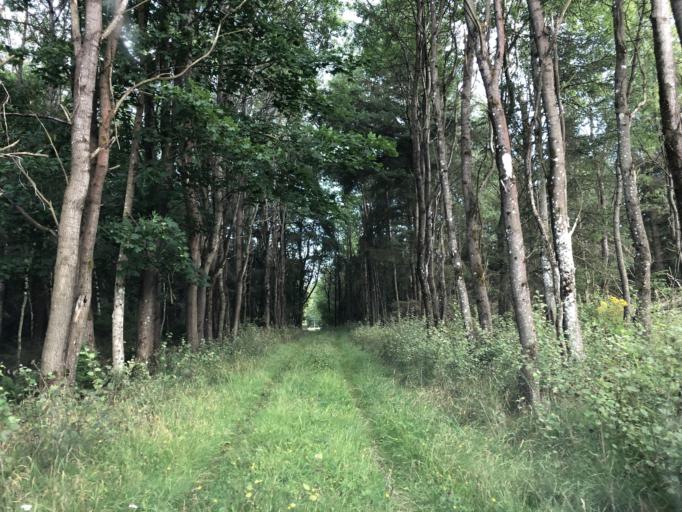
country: DK
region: Central Jutland
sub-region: Holstebro Kommune
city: Ulfborg
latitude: 56.2804
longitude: 8.4243
